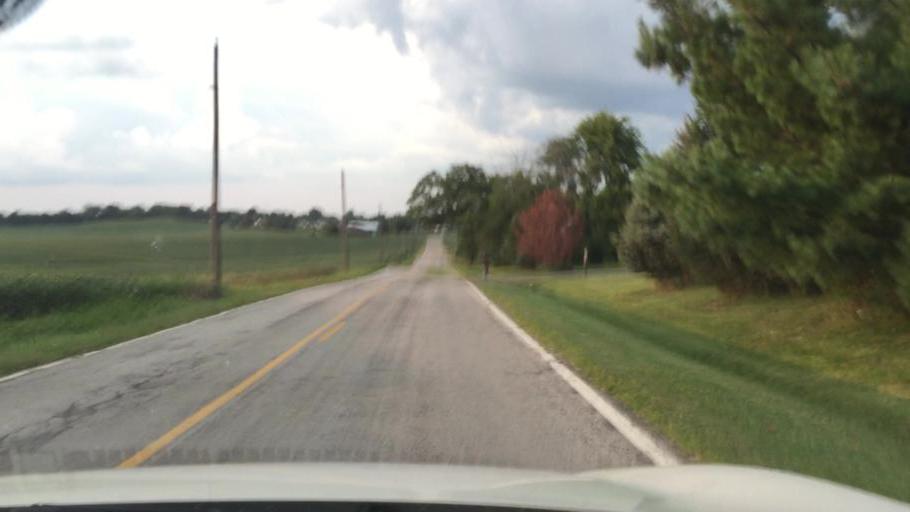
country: US
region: Ohio
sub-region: Champaign County
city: Mechanicsburg
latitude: 40.0125
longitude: -83.5917
